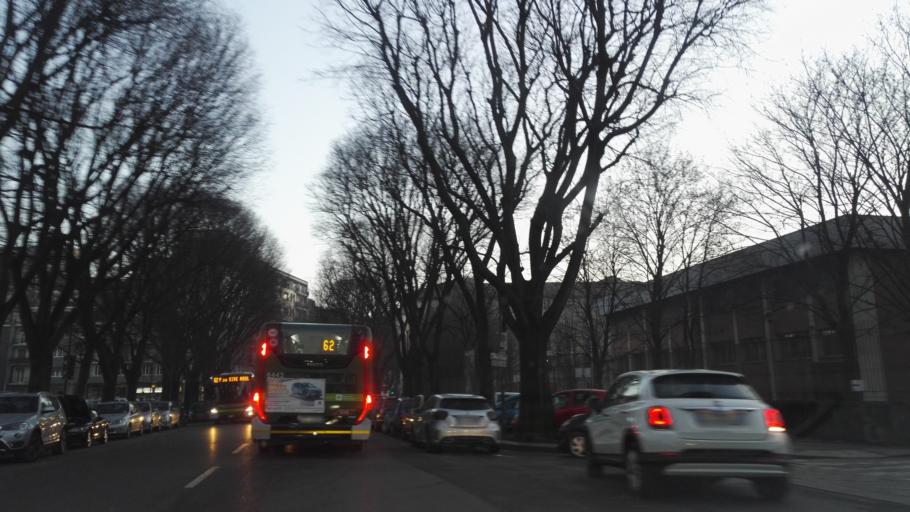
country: IT
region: Lombardy
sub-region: Citta metropolitana di Milano
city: Milano
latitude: 45.4603
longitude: 9.2143
